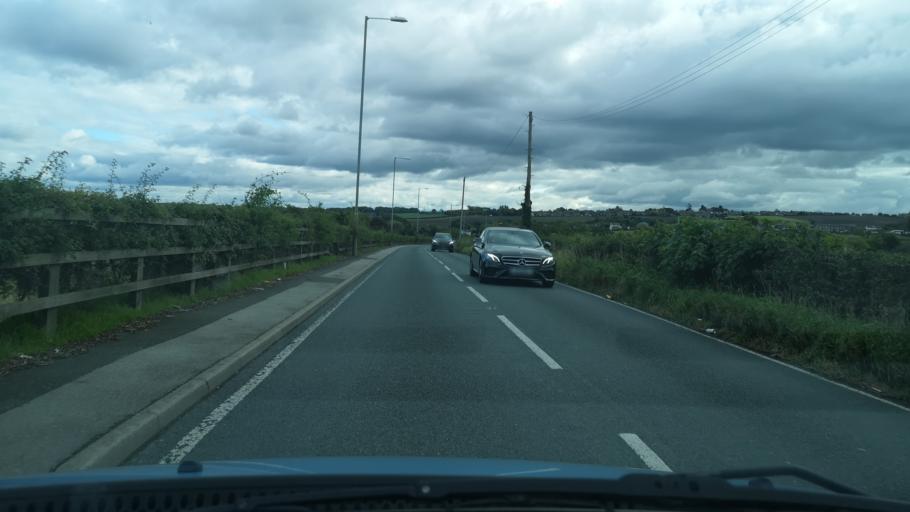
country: GB
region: England
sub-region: City and Borough of Wakefield
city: Middlestown
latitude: 53.6595
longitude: -1.5891
